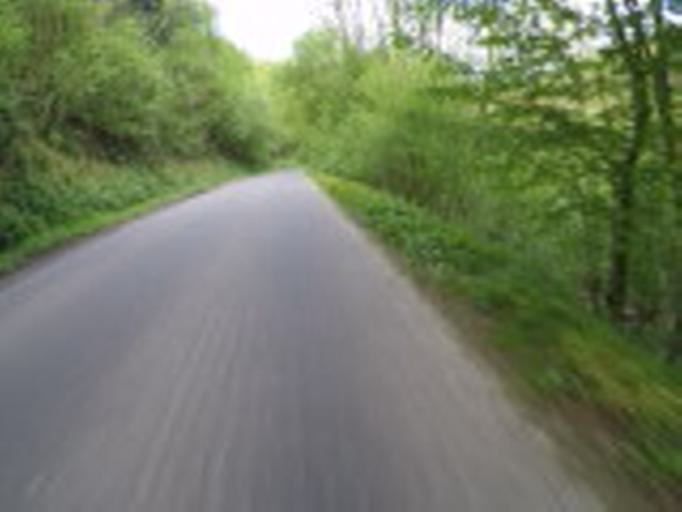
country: BE
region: Wallonia
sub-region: Province de Namur
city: Yvoir
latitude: 50.3463
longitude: 4.9410
